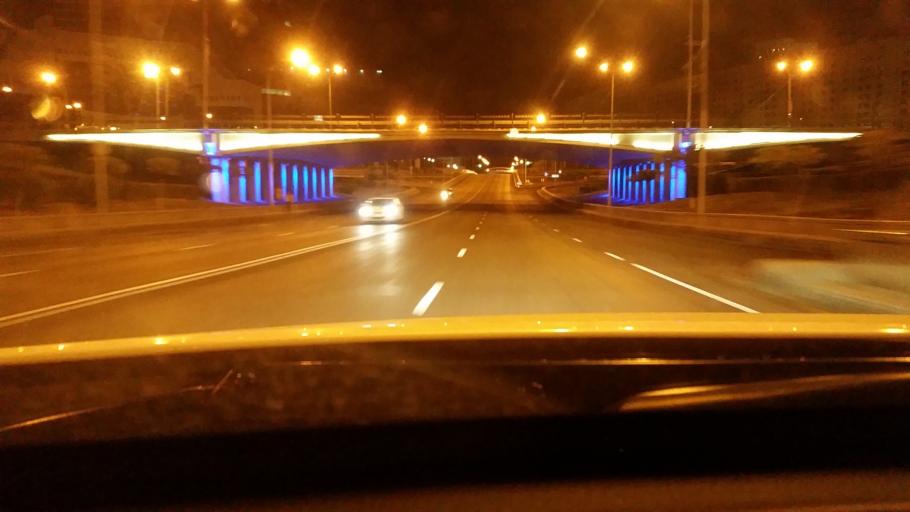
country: KZ
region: Astana Qalasy
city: Astana
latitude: 51.1212
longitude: 71.4362
